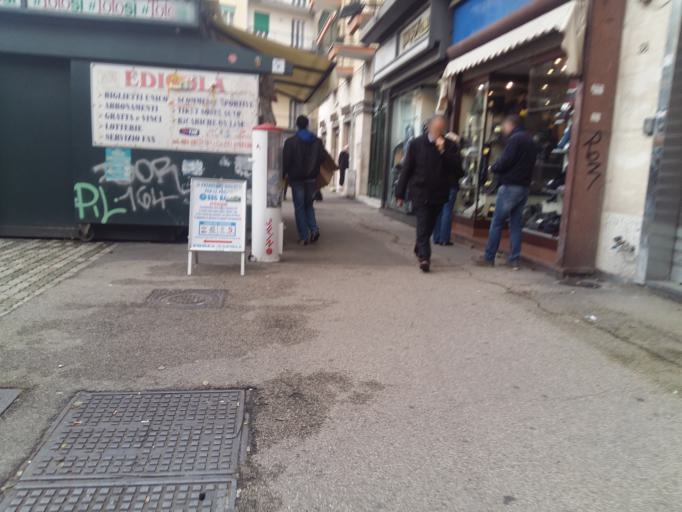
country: IT
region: Campania
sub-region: Provincia di Napoli
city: Napoli
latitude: 40.8502
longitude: 14.2313
